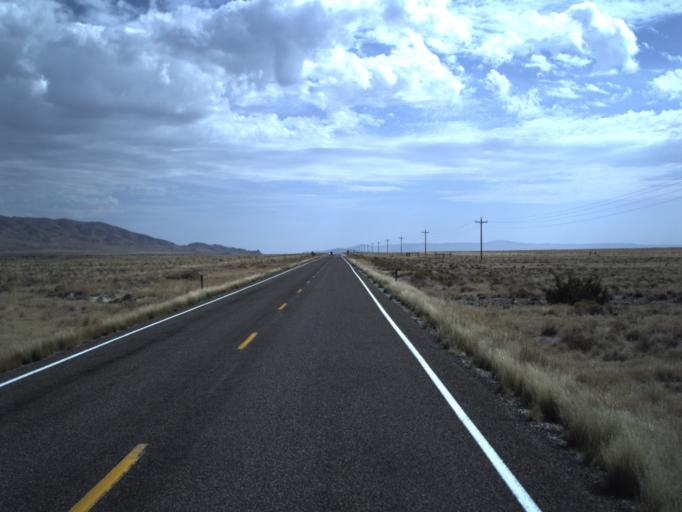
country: US
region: Utah
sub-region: Tooele County
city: Wendover
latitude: 41.4296
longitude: -113.8126
